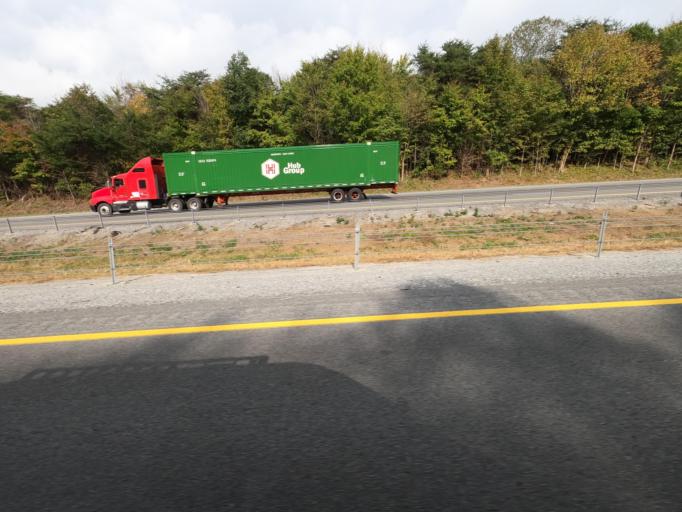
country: US
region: Tennessee
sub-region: Williamson County
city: Fairview
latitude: 36.0246
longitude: -87.1830
